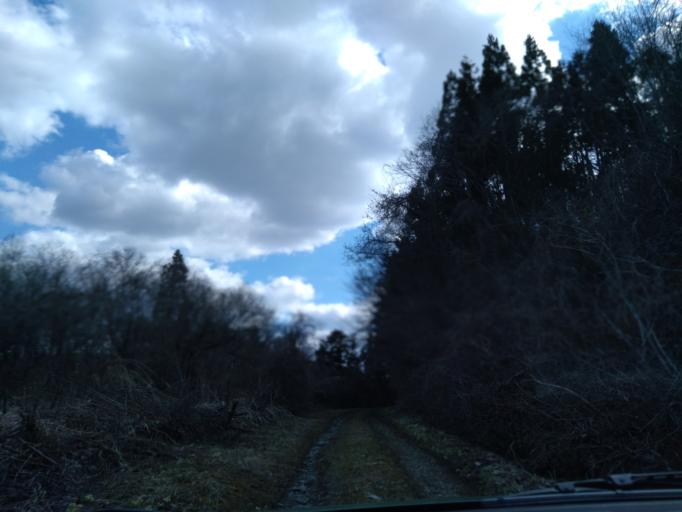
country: JP
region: Iwate
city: Ichinoseki
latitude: 38.9820
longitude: 141.0186
